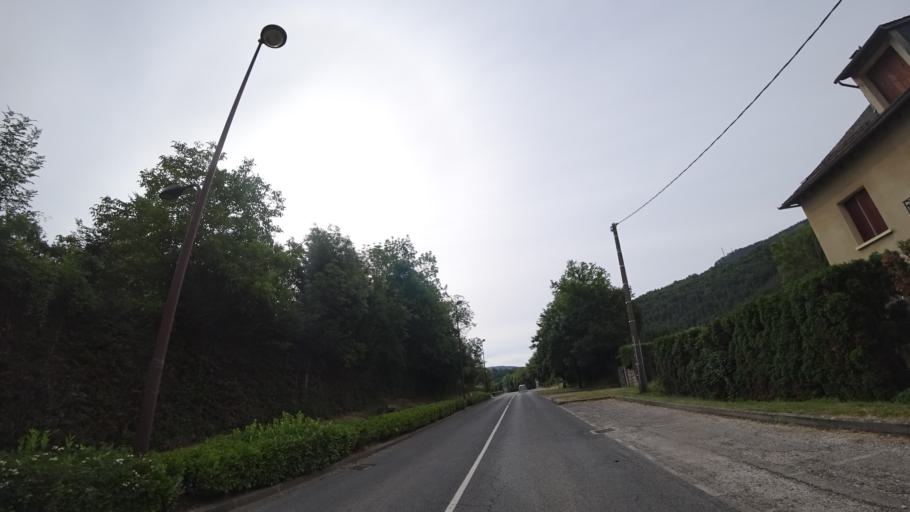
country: FR
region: Languedoc-Roussillon
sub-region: Departement de la Lozere
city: La Canourgue
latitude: 44.4353
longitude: 3.2035
